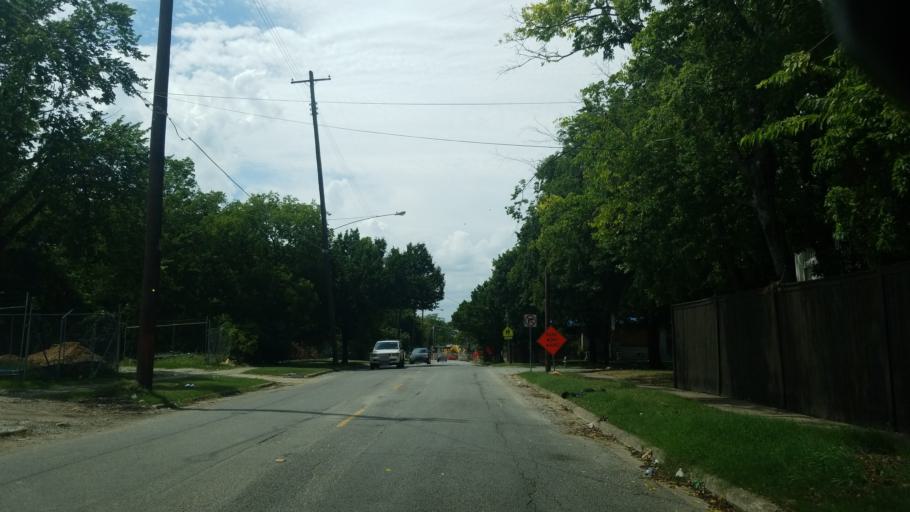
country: US
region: Texas
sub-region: Dallas County
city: Dallas
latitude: 32.7925
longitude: -96.7686
